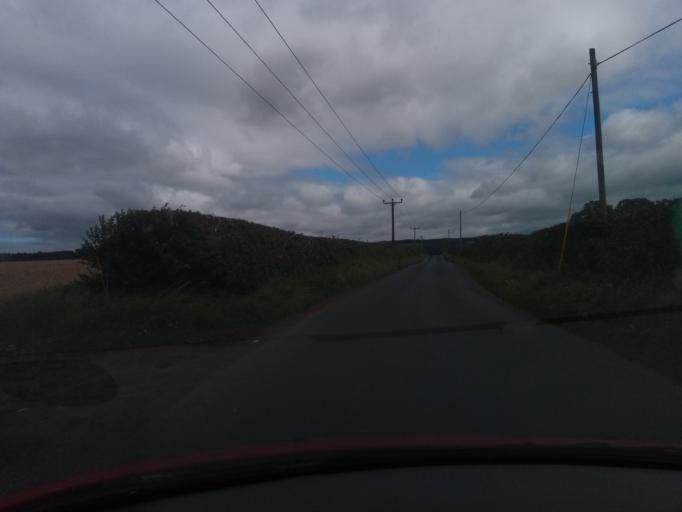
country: GB
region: Scotland
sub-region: The Scottish Borders
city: Kelso
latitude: 55.5309
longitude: -2.4598
